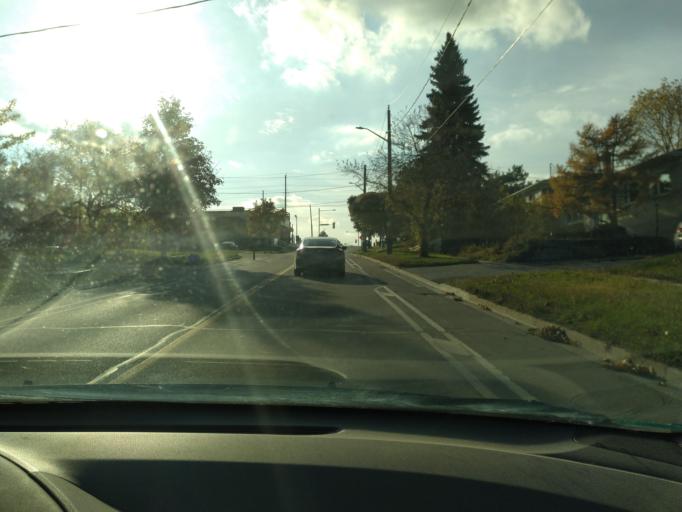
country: CA
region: Ontario
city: Newmarket
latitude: 44.0512
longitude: -79.4773
